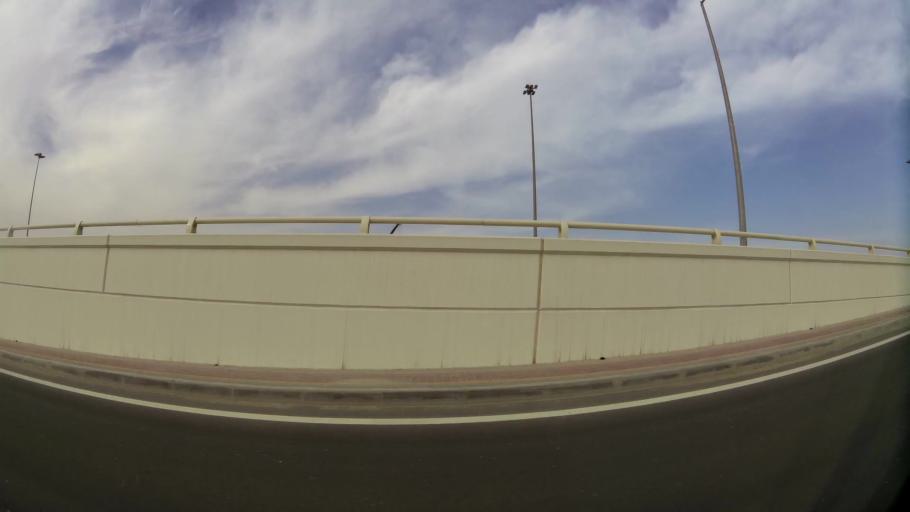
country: QA
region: Baladiyat ar Rayyan
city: Ar Rayyan
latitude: 25.3183
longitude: 51.3568
